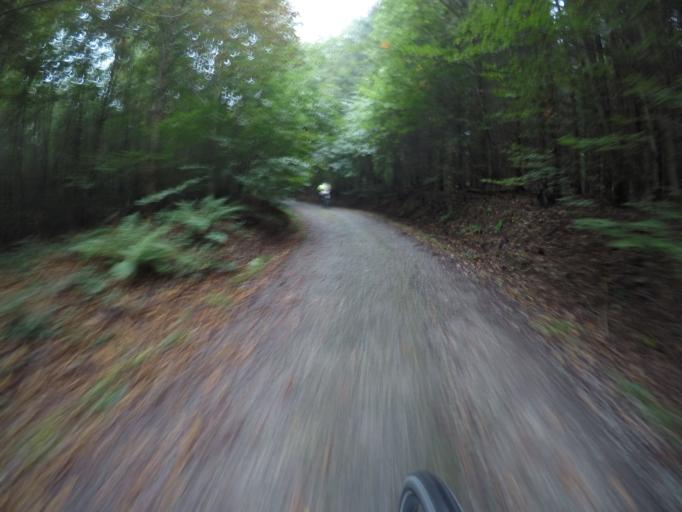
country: DE
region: Baden-Wuerttemberg
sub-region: Regierungsbezirk Stuttgart
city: Gerlingen
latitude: 48.7572
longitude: 9.0494
